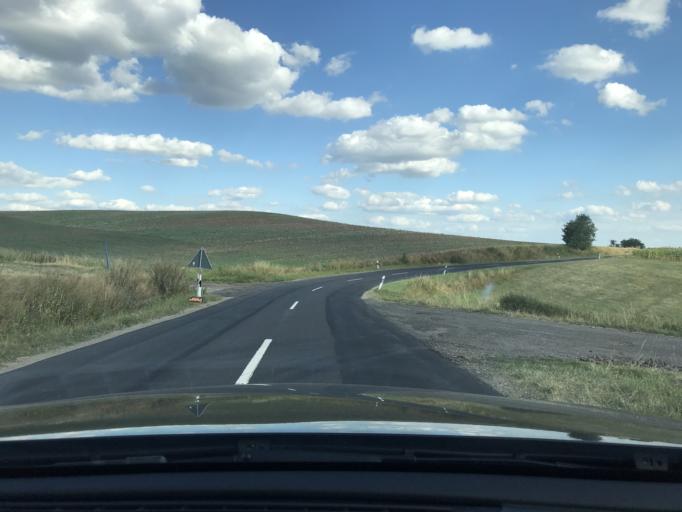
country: DE
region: Bavaria
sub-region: Regierungsbezirk Unterfranken
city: Kirchlauter
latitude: 50.0698
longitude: 10.6669
